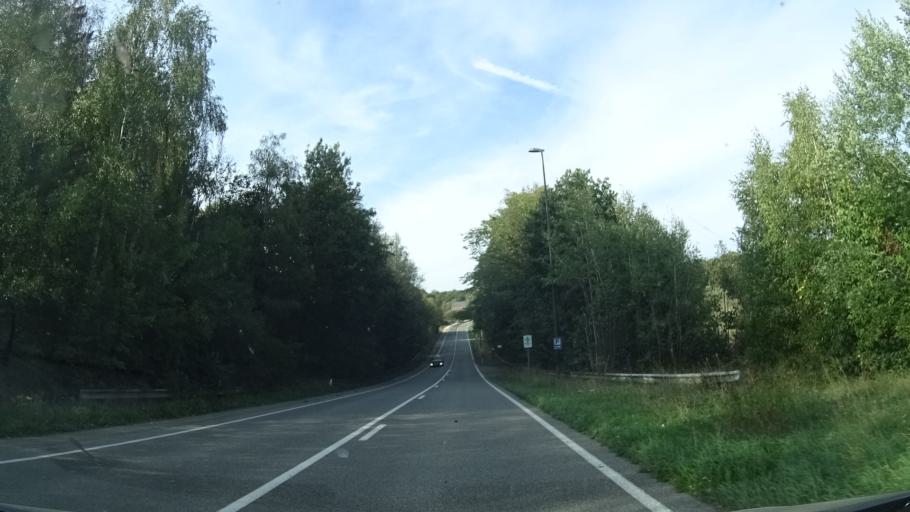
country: BE
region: Wallonia
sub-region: Province de Namur
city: Cerfontaine
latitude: 50.1976
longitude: 4.3769
